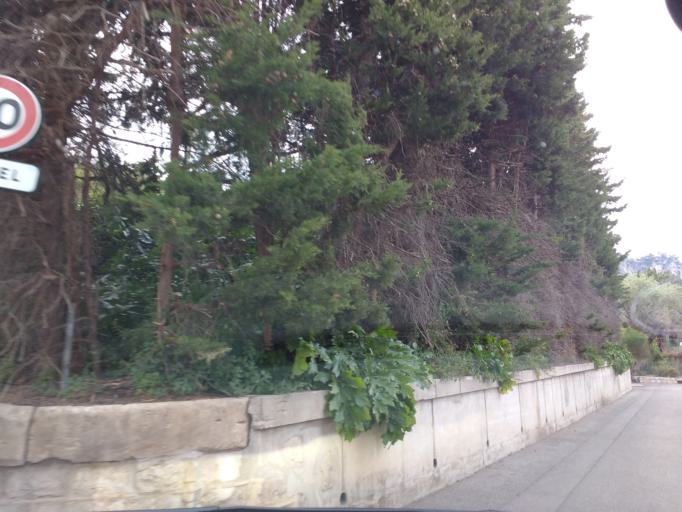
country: FR
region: Provence-Alpes-Cote d'Azur
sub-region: Departement des Alpes-Maritimes
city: Beaulieu-sur-Mer
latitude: 43.7044
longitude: 7.3307
